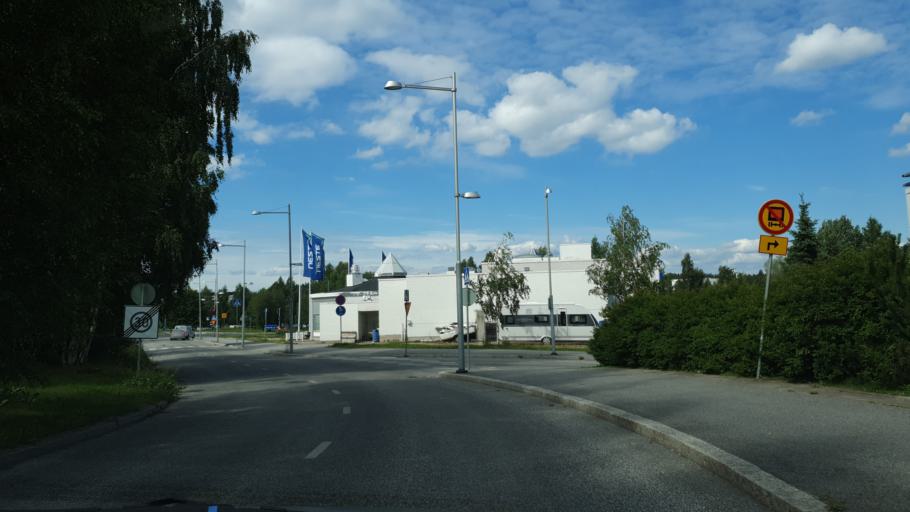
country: FI
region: Kainuu
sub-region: Kajaani
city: Kajaani
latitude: 64.2206
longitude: 27.7424
